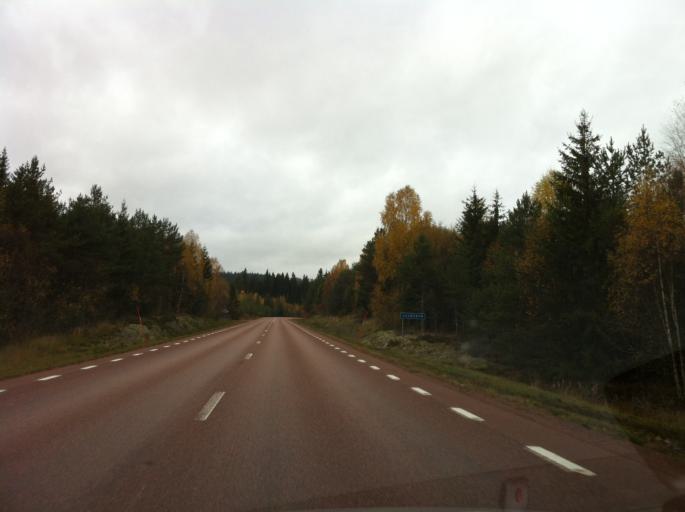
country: SE
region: Dalarna
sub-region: Alvdalens Kommun
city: AElvdalen
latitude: 61.2697
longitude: 13.8145
